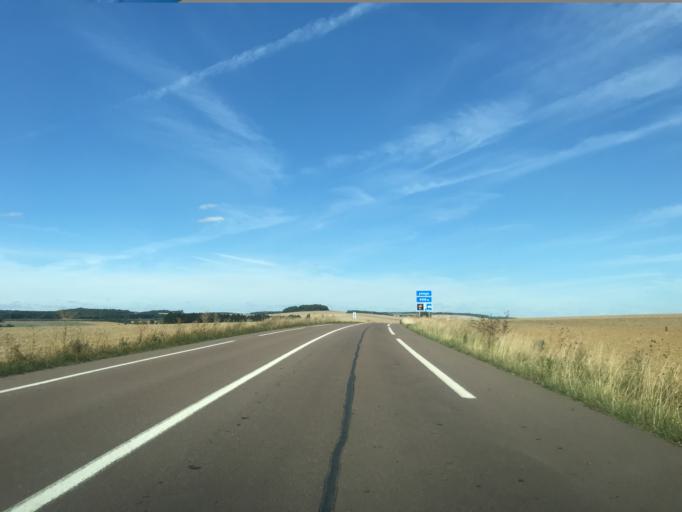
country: FR
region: Champagne-Ardenne
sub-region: Departement de la Marne
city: Chatillon-sur-Marne
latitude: 49.1495
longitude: 3.7145
